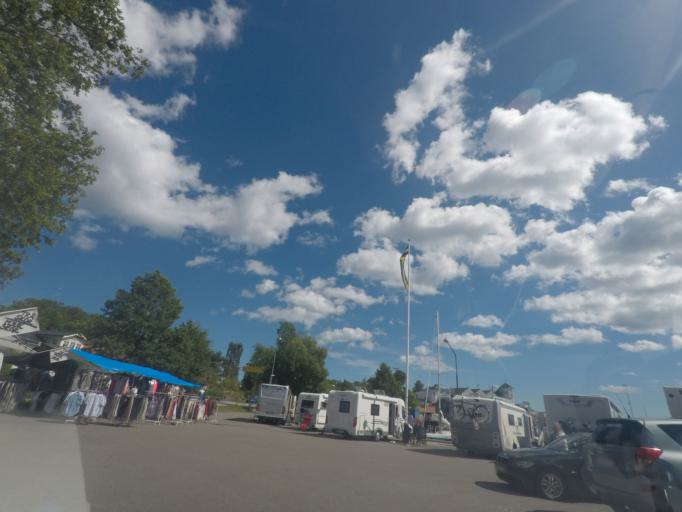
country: SE
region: Stockholm
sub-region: Norrtalje Kommun
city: Arno
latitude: 60.0999
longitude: 18.8106
